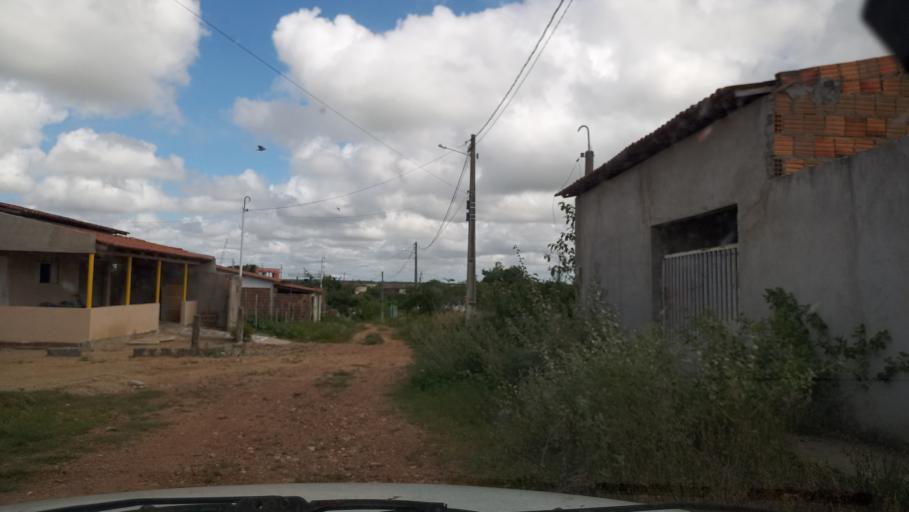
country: BR
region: Rio Grande do Norte
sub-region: Brejinho
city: Brejinho
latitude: -6.1463
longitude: -35.4302
